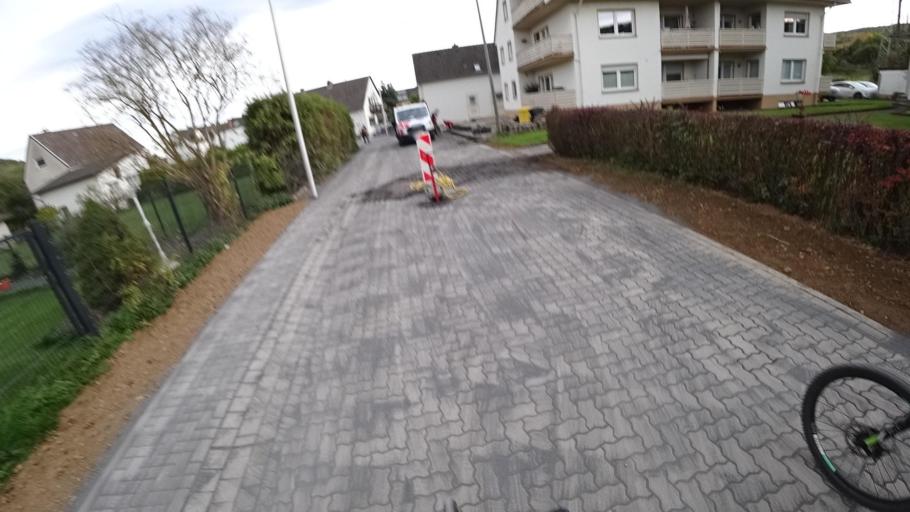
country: DE
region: Rheinland-Pfalz
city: Konigsfeld
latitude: 50.5441
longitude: 7.1689
